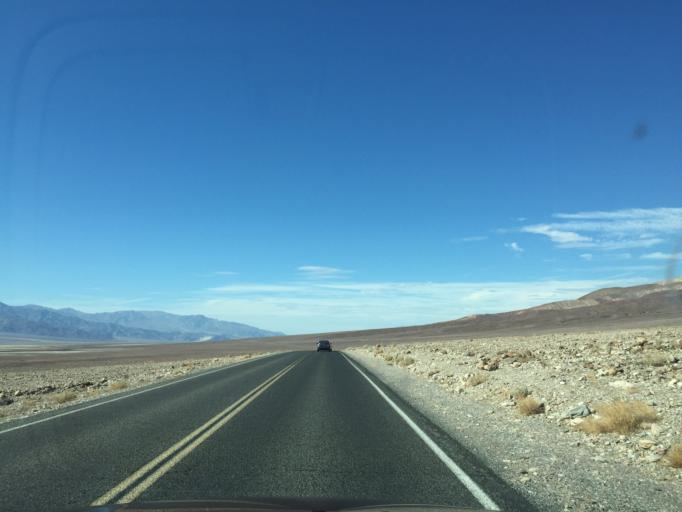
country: US
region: Nevada
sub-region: Nye County
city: Beatty
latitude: 36.2584
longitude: -116.7778
